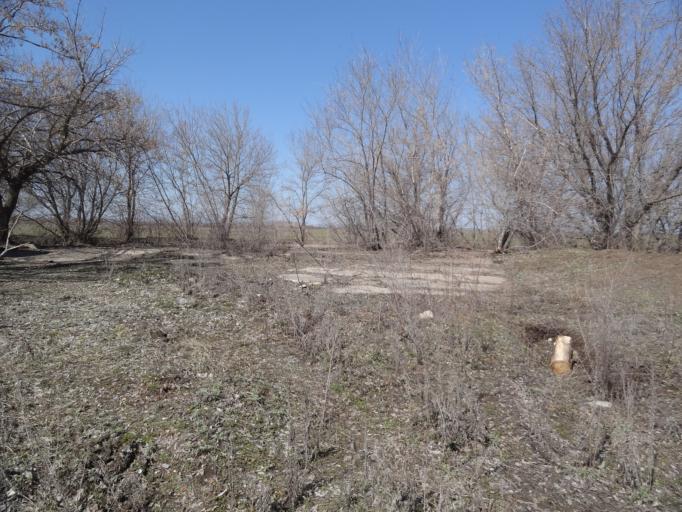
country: RU
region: Saratov
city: Shumeyka
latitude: 51.4200
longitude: 46.2857
